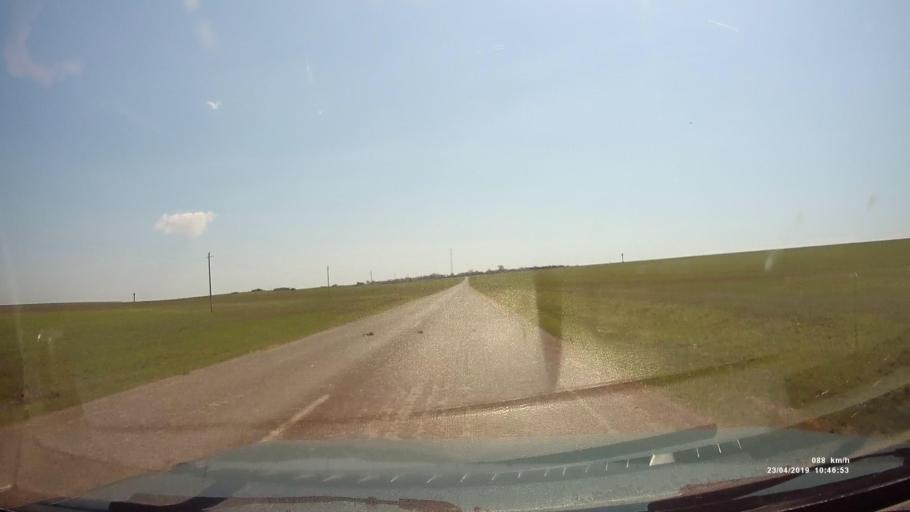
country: RU
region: Kalmykiya
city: Yashalta
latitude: 46.4391
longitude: 42.6987
